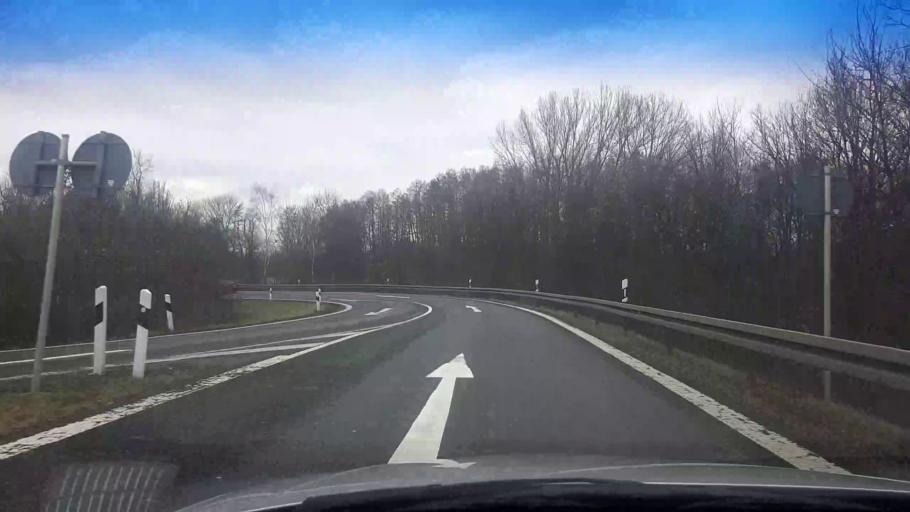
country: DE
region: Bavaria
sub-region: Regierungsbezirk Unterfranken
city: Knetzgau
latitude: 49.9789
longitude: 10.5597
